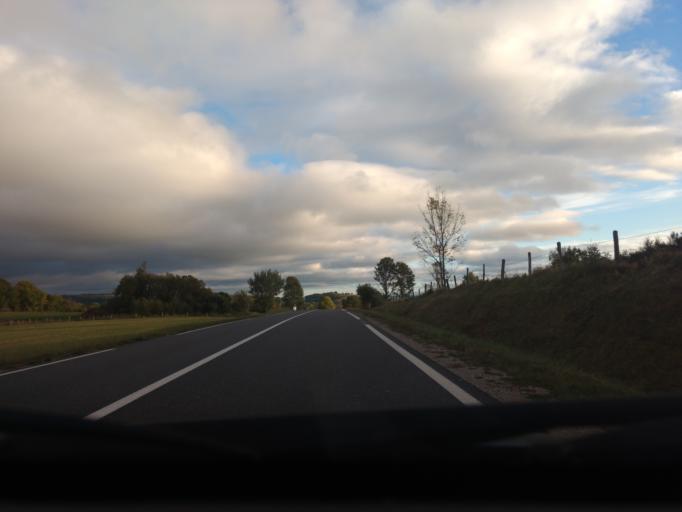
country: FR
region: Midi-Pyrenees
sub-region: Departement de l'Aveyron
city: Laguiole
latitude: 44.6540
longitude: 2.8501
